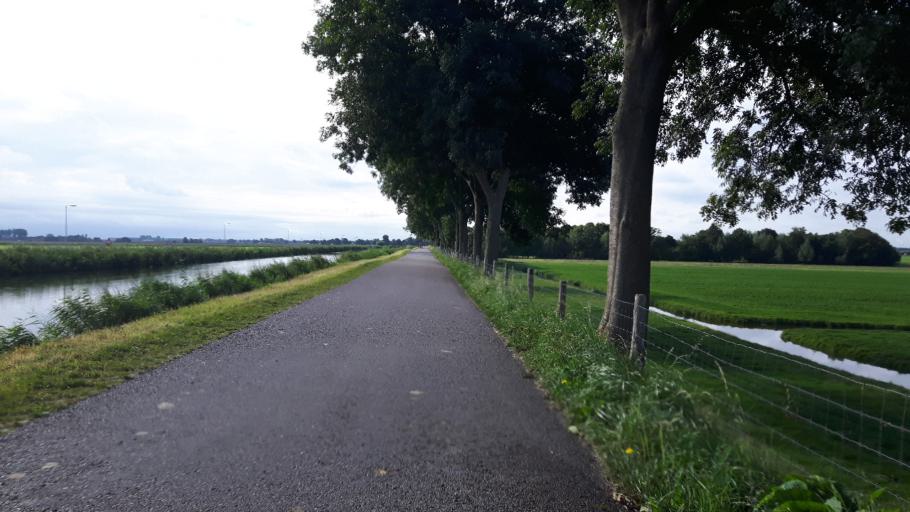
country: NL
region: North Holland
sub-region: Gemeente Purmerend
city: Purmerend
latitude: 52.5580
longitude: 4.9767
